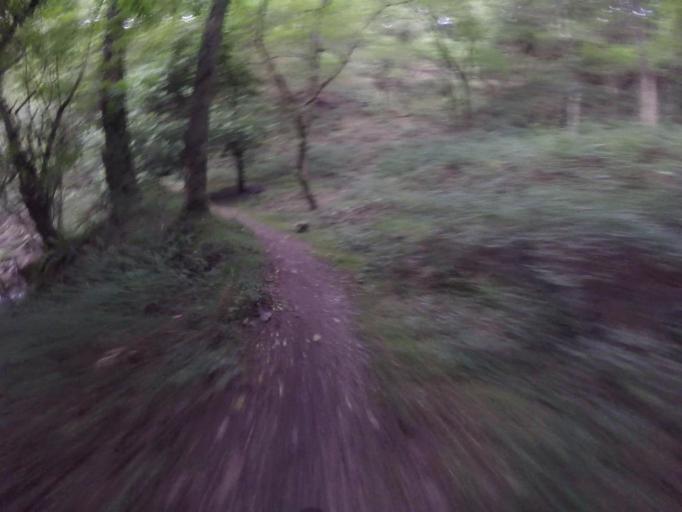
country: ES
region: Basque Country
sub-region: Provincia de Guipuzcoa
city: Errenteria
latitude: 43.2751
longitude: -1.8414
